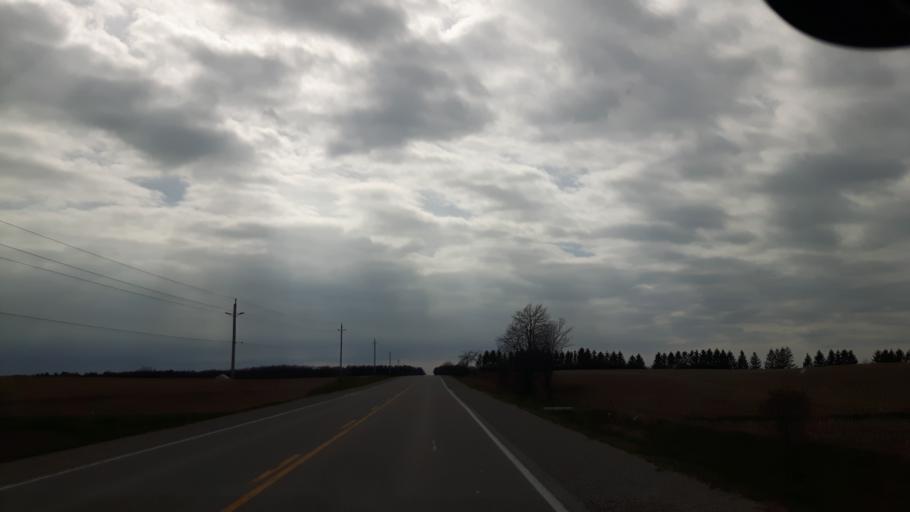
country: CA
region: Ontario
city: Bluewater
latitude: 43.5869
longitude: -81.6505
